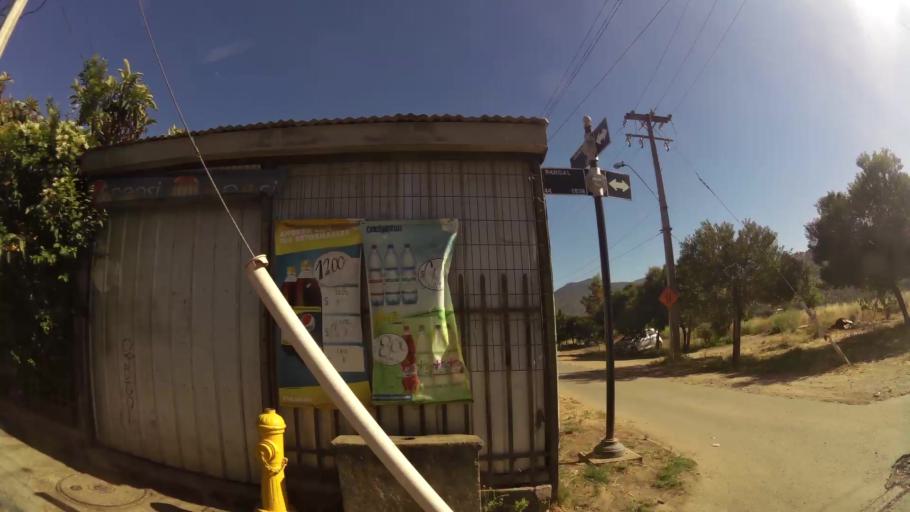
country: CL
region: Santiago Metropolitan
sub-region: Provincia de Chacabuco
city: Lampa
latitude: -33.4059
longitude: -71.1266
